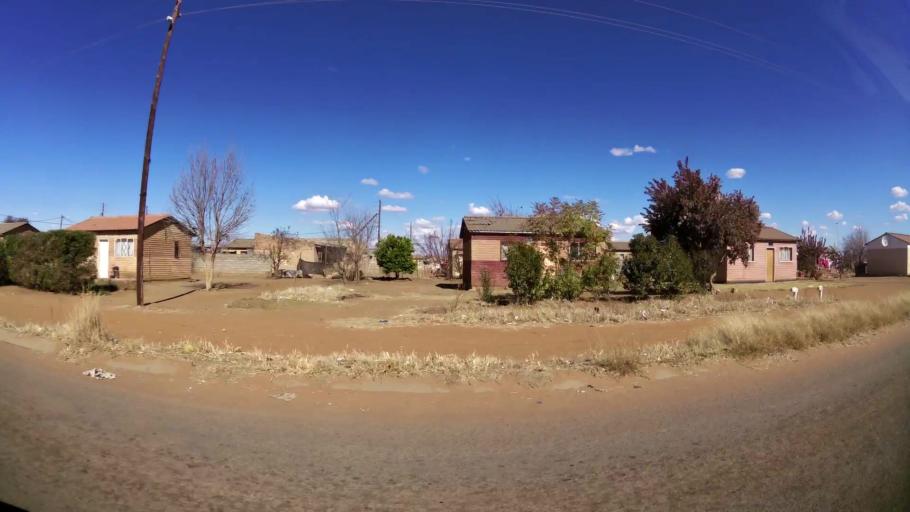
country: ZA
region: North-West
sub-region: Dr Kenneth Kaunda District Municipality
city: Klerksdorp
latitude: -26.8683
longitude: 26.5749
